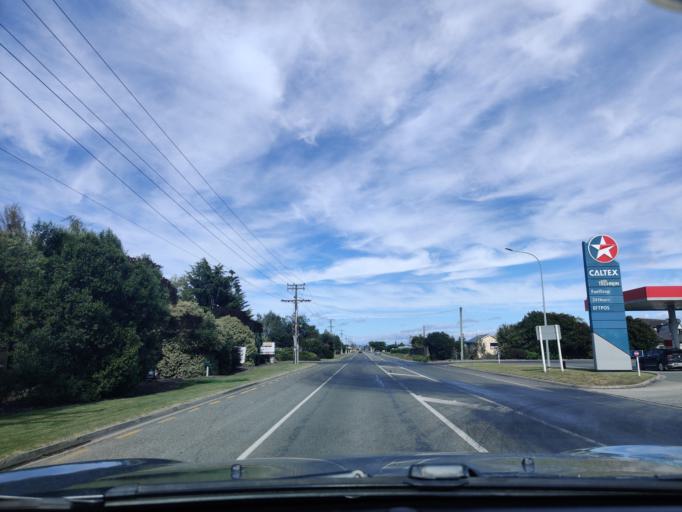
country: NZ
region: Tasman
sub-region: Tasman District
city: Richmond
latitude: -41.3484
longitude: 173.1631
